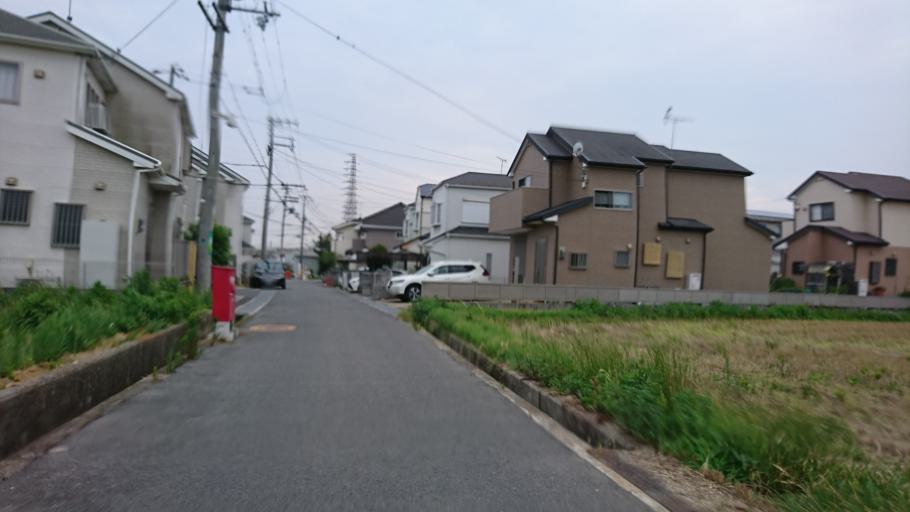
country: JP
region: Hyogo
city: Kakogawacho-honmachi
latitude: 34.7321
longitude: 134.8941
